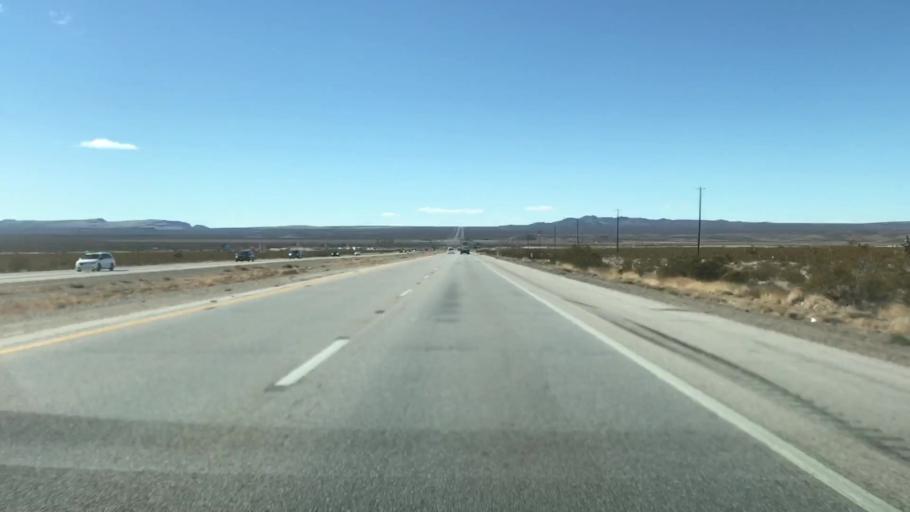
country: US
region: Nevada
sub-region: Clark County
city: Sandy Valley
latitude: 35.4501
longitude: -115.6577
